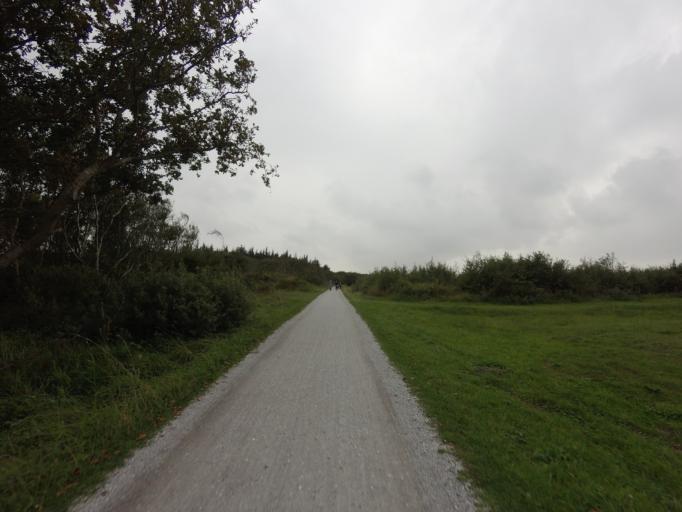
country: NL
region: Friesland
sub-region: Gemeente Schiermonnikoog
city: Schiermonnikoog
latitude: 53.4898
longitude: 6.1632
